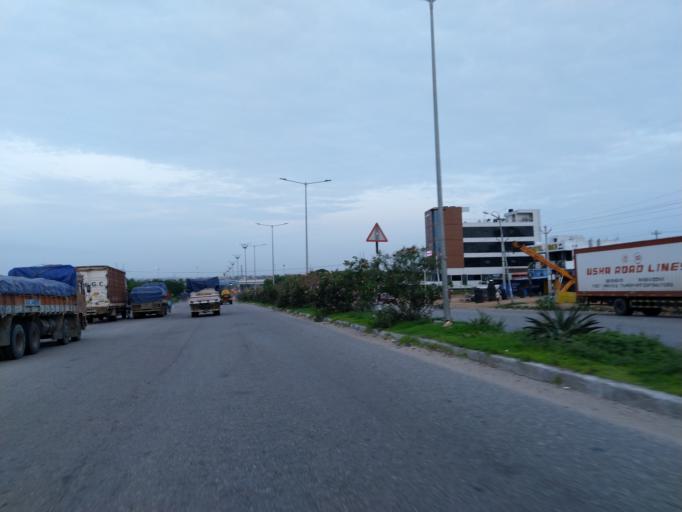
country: IN
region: Telangana
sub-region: Rangareddi
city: Lal Bahadur Nagar
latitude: 17.3174
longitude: 78.6622
